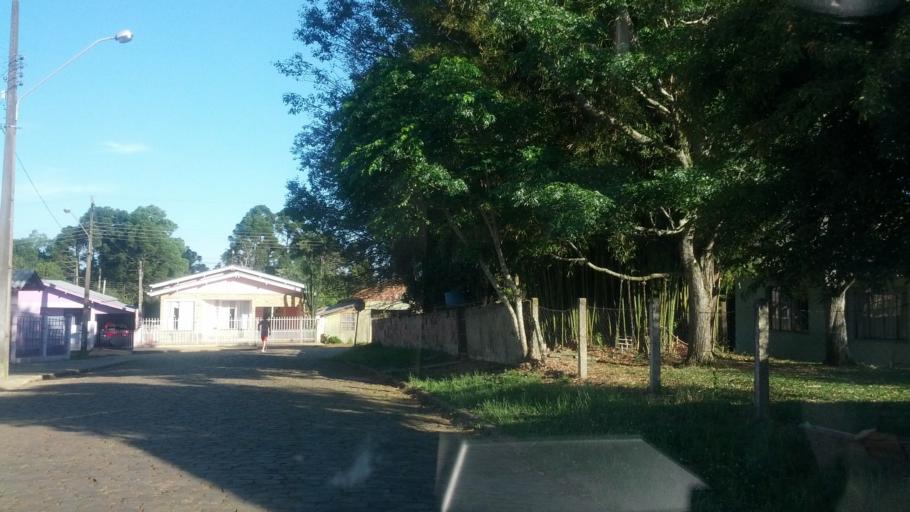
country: BR
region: Rio Grande do Sul
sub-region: Vacaria
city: Estrela
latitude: -27.9005
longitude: -50.7616
